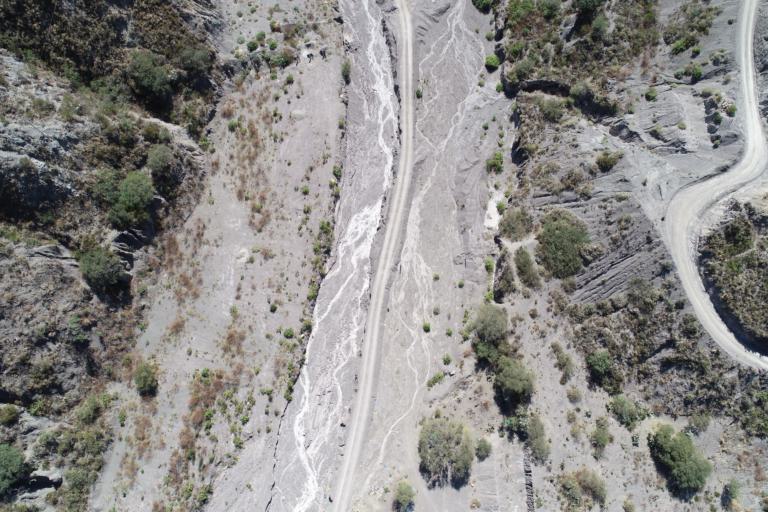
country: BO
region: La Paz
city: La Paz
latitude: -16.6255
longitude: -68.0414
